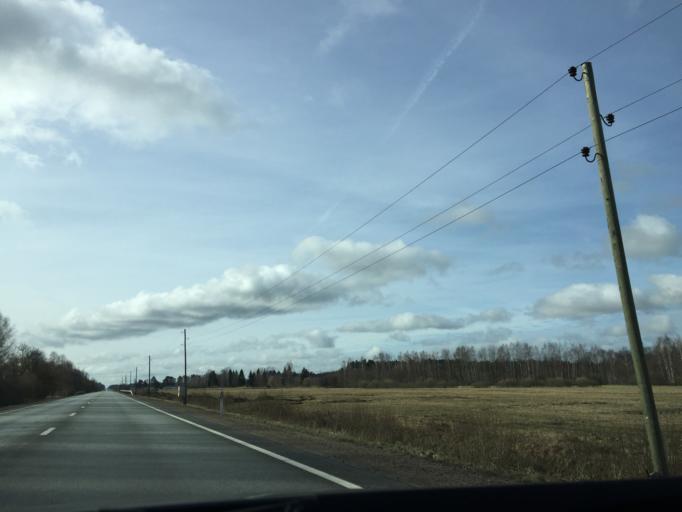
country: LV
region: Jelgava
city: Jelgava
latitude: 56.6014
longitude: 23.7200
